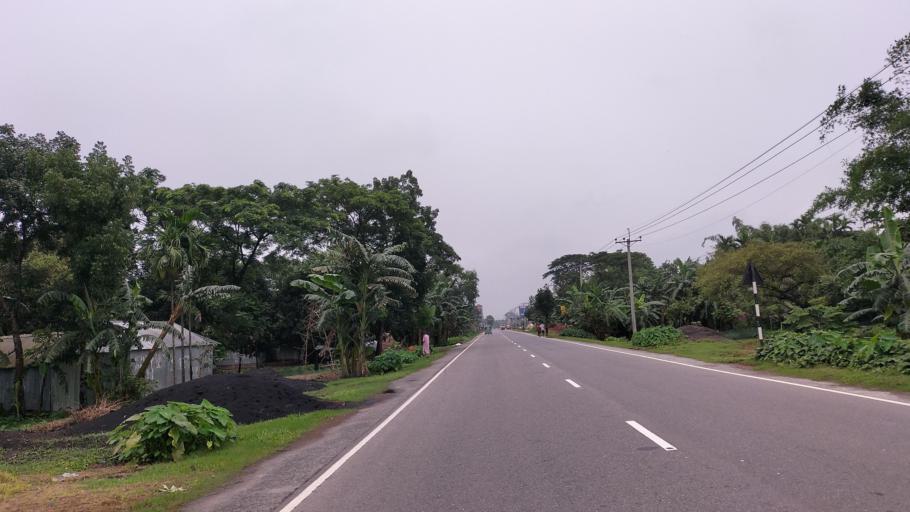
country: BD
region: Dhaka
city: Netrakona
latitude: 24.8513
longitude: 90.6236
